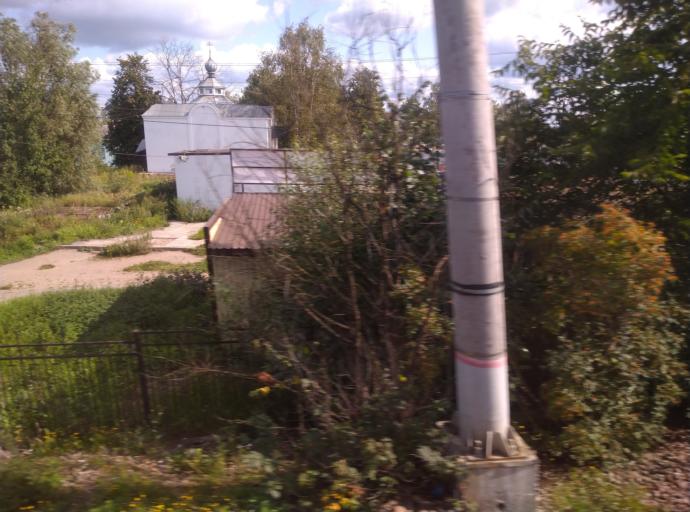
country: RU
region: Leningrad
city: Ul'yanovka
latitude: 59.6361
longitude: 30.7567
